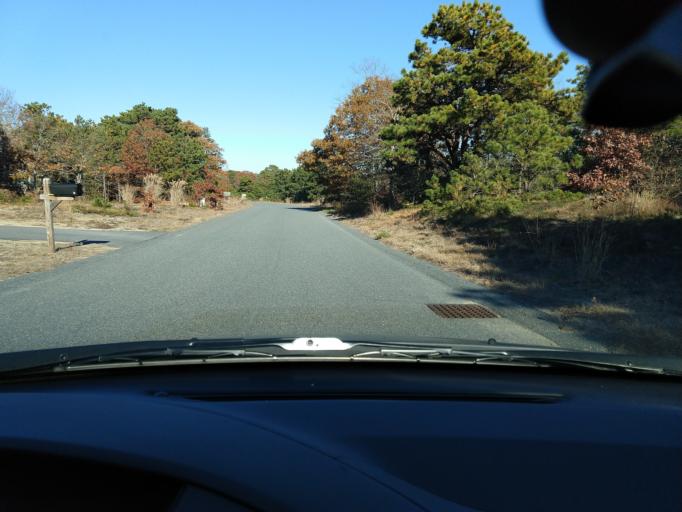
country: US
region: Massachusetts
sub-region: Barnstable County
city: North Eastham
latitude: 41.8715
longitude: -69.9937
